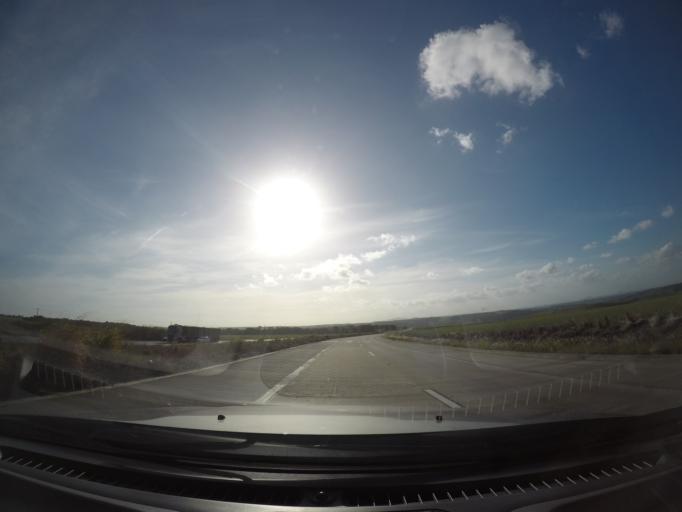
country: BR
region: Alagoas
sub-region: Pilar
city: Pilar
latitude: -9.5867
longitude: -35.9794
